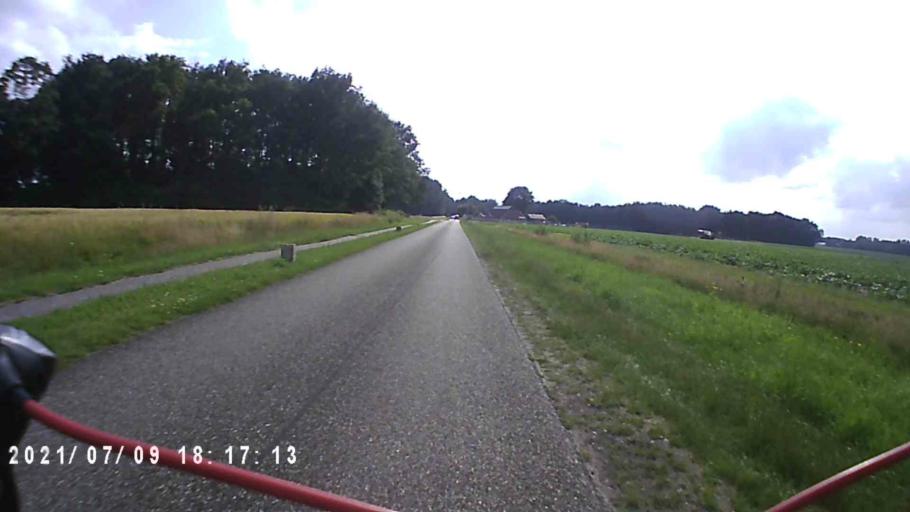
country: NL
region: Groningen
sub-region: Gemeente Pekela
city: Oude Pekela
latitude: 53.0530
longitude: 7.0116
